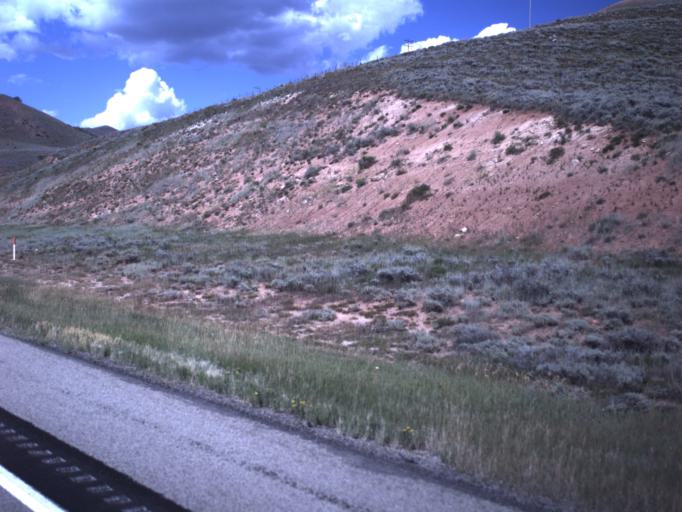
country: US
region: Utah
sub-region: Wasatch County
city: Heber
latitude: 40.2060
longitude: -111.1043
